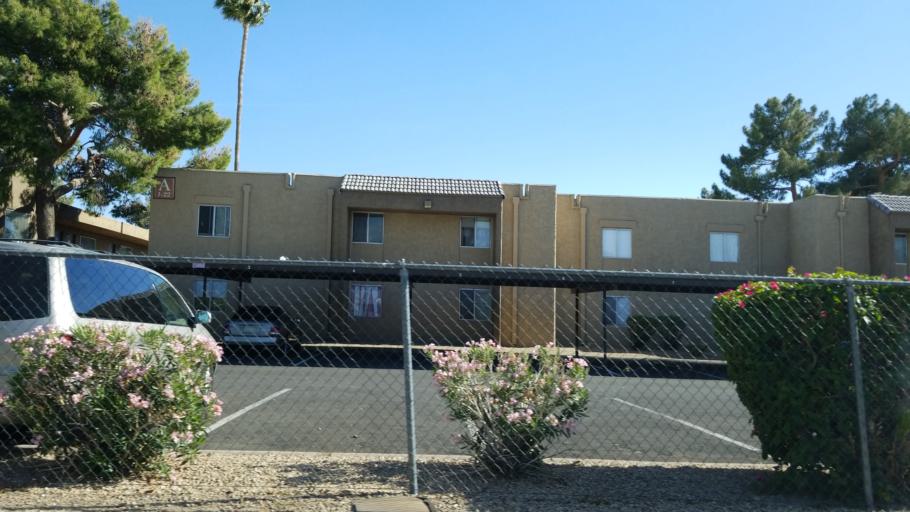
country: US
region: Arizona
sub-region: Maricopa County
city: Phoenix
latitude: 33.5196
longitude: -112.0958
